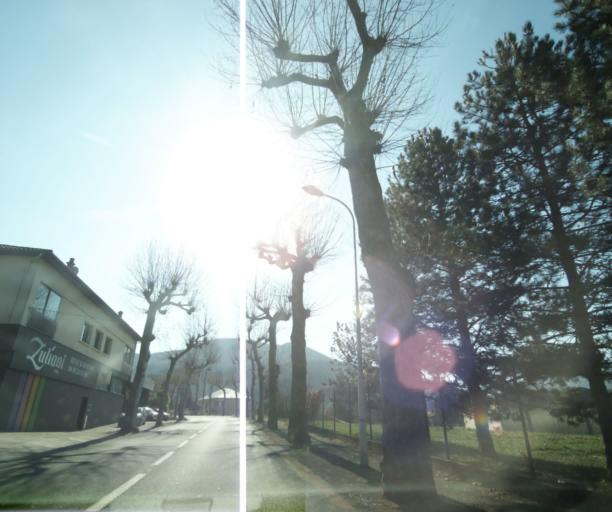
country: FR
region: Midi-Pyrenees
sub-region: Departement de l'Aveyron
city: Saint-Affrique
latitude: 43.9496
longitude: 2.8982
